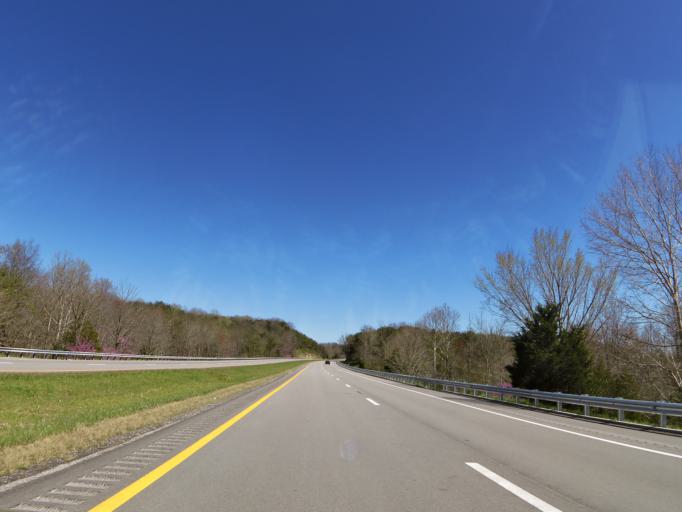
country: US
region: Kentucky
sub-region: Pulaski County
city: Somerset
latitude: 37.0980
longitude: -84.8356
